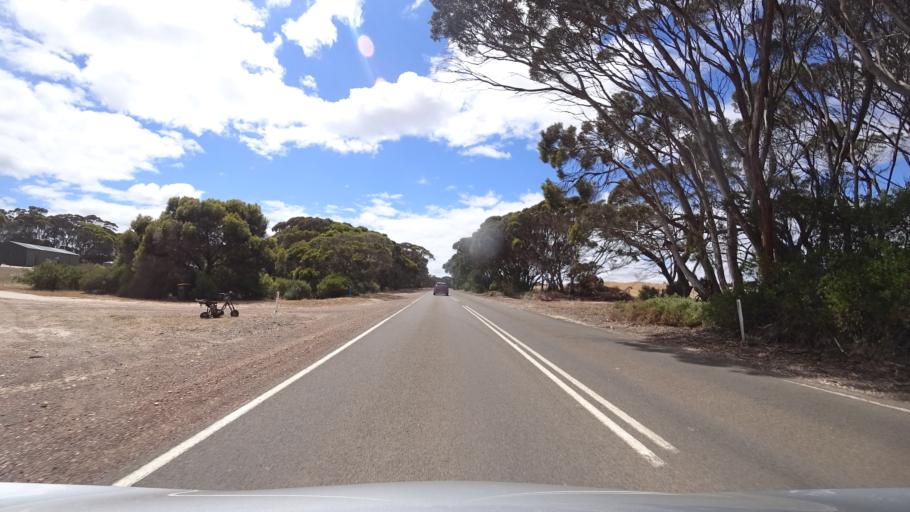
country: AU
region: South Australia
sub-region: Kangaroo Island
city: Kingscote
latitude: -35.6516
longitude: 137.5661
